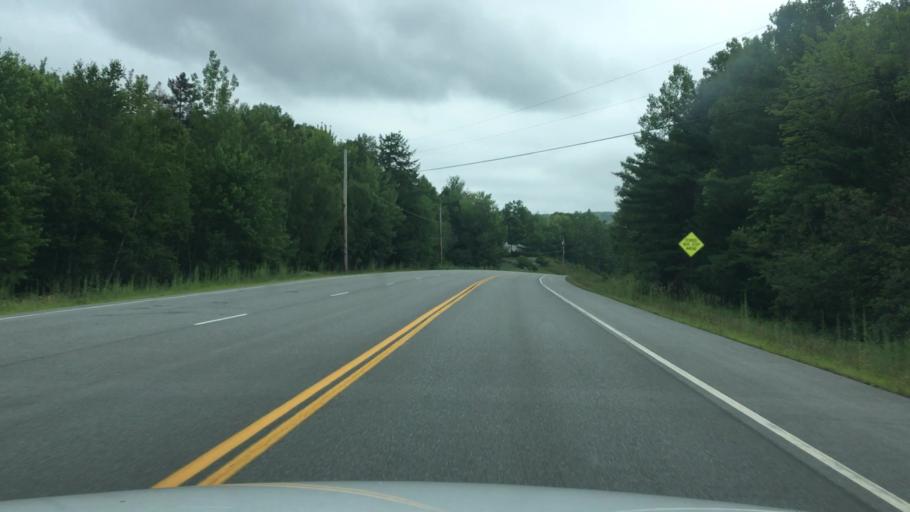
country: US
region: Maine
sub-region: Penobscot County
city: Bradley
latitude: 44.8235
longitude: -68.4935
